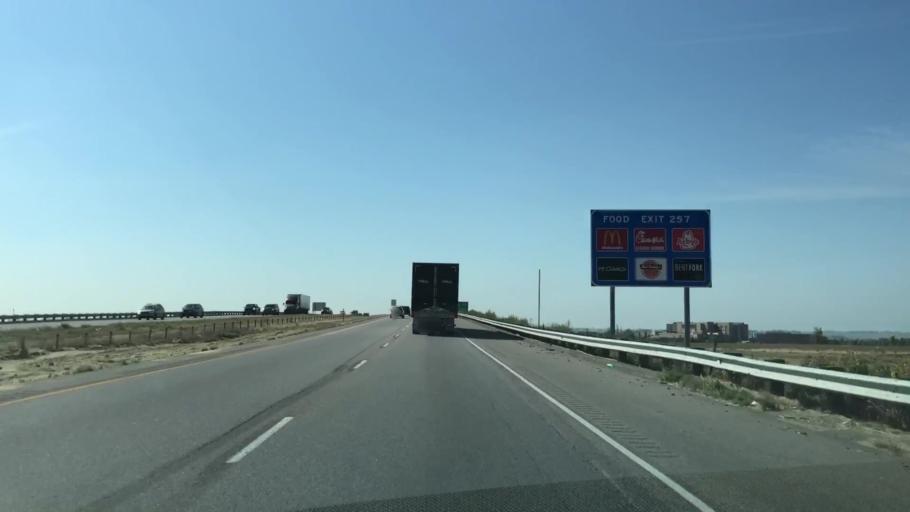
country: US
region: Colorado
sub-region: Larimer County
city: Loveland
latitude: 40.4262
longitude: -104.9927
